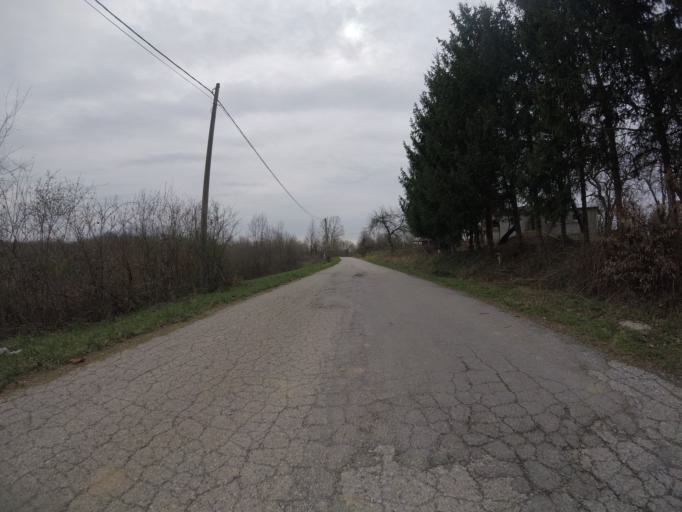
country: HR
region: Zagrebacka
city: Lukavec
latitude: 45.5765
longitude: 15.9638
